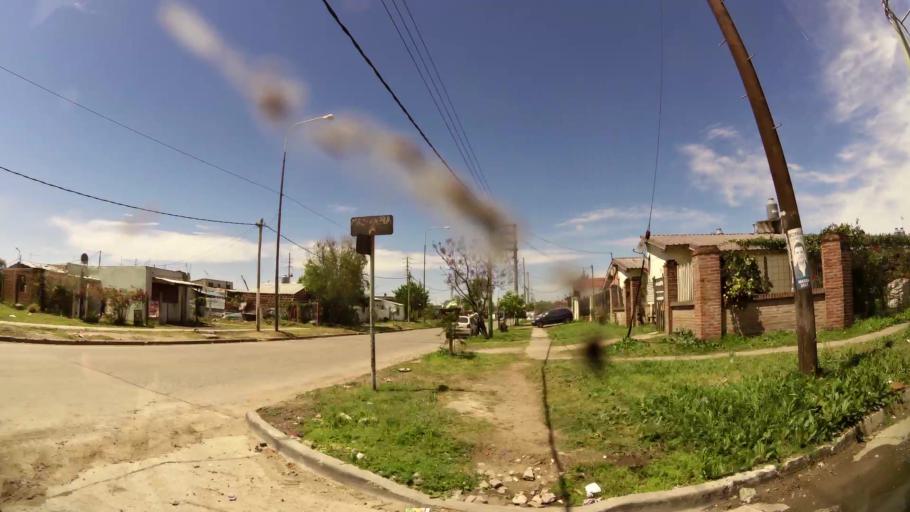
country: AR
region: Buenos Aires
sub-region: Partido de Quilmes
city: Quilmes
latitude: -34.7443
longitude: -58.3129
